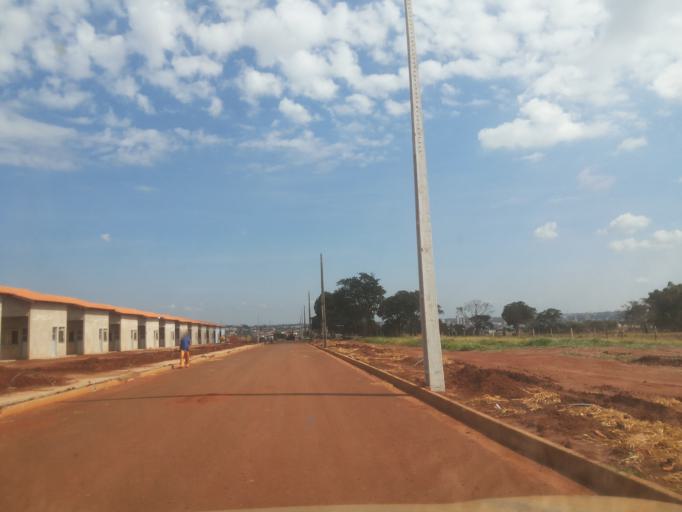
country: BR
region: Minas Gerais
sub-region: Ituiutaba
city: Ituiutaba
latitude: -18.9755
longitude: -49.4366
